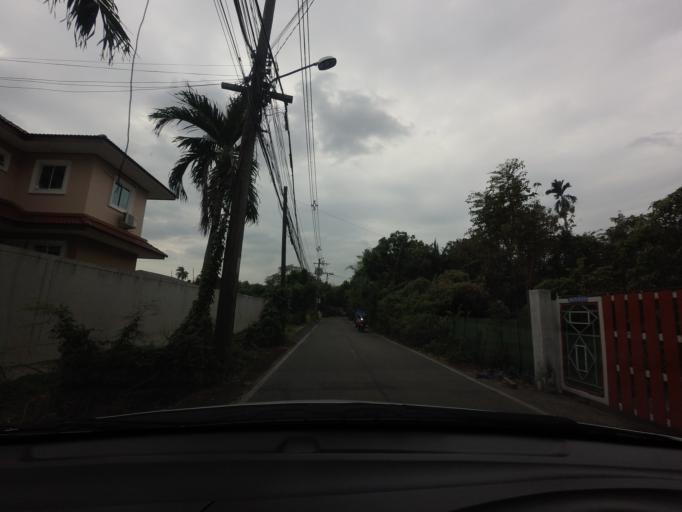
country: TH
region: Bangkok
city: Yan Nawa
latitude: 13.6930
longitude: 100.5605
